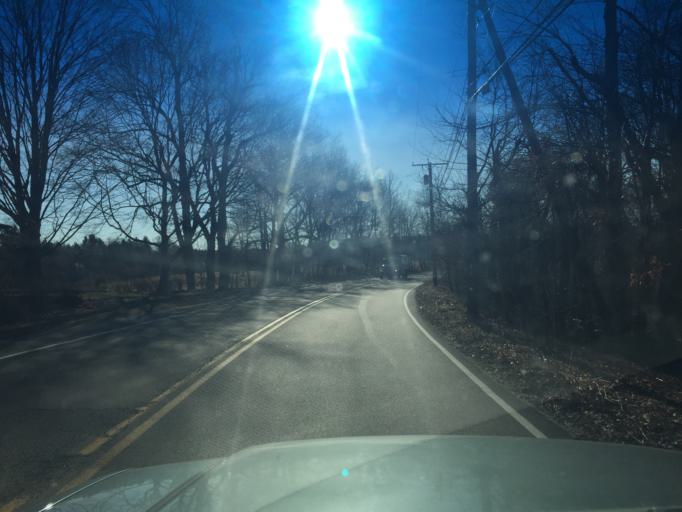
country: US
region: Massachusetts
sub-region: Norfolk County
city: Millis
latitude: 42.1840
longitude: -71.3637
